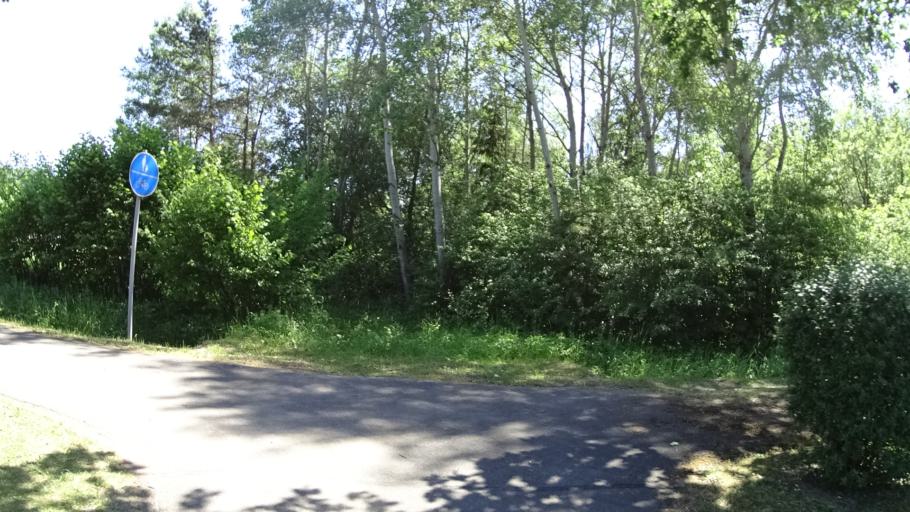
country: DE
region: Bavaria
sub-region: Regierungsbezirk Mittelfranken
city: Pleinfeld
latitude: 49.1093
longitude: 10.9257
